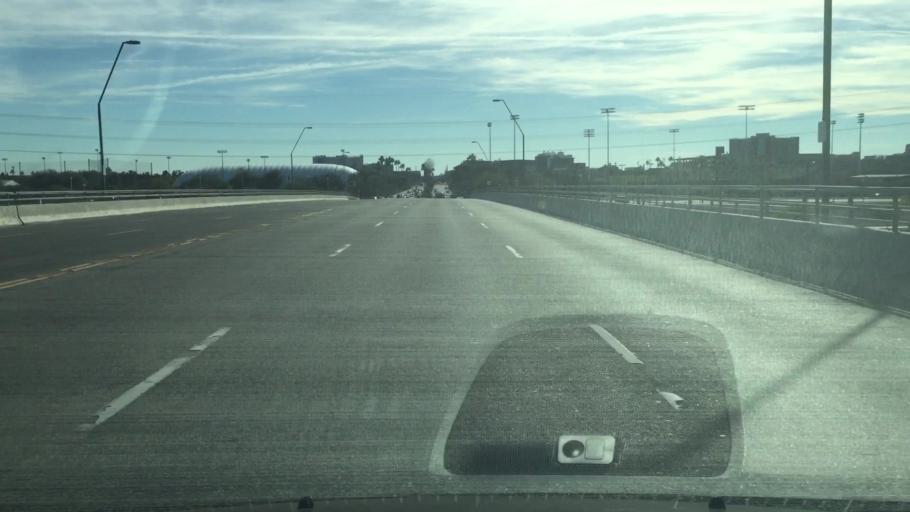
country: US
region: Arizona
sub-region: Maricopa County
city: Tempe
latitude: 33.4313
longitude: -111.9263
